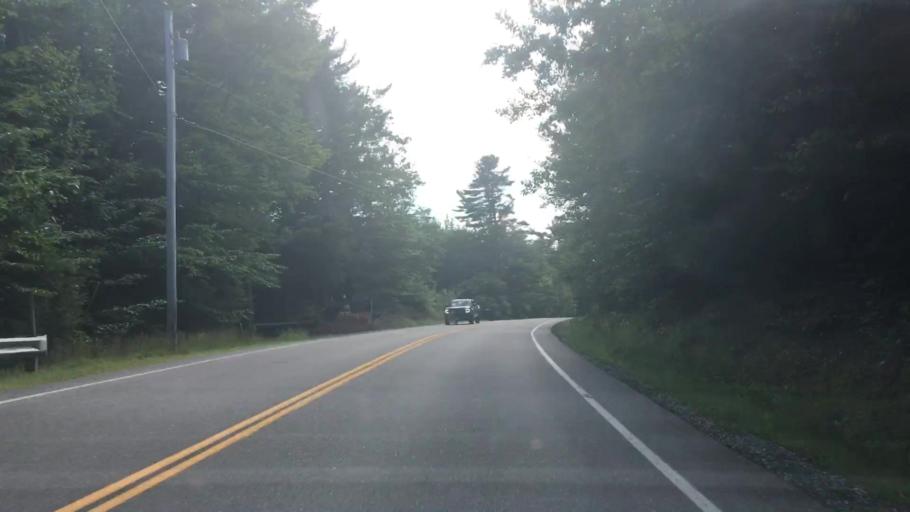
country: US
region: Maine
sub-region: Androscoggin County
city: Poland
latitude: 44.0129
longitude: -70.4466
